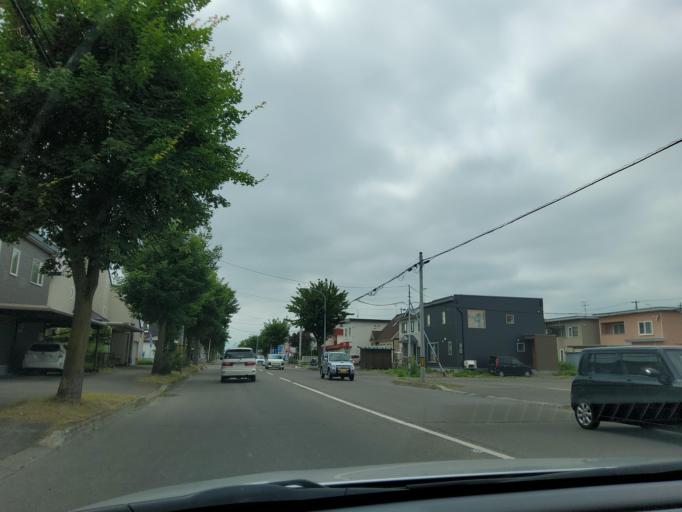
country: JP
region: Hokkaido
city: Obihiro
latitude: 42.9147
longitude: 143.1719
